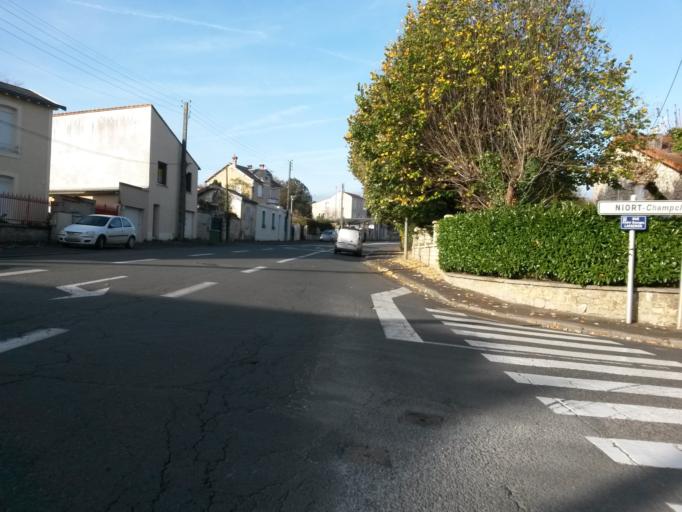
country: FR
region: Poitou-Charentes
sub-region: Departement des Deux-Sevres
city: Niort
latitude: 46.3167
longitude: -0.4422
